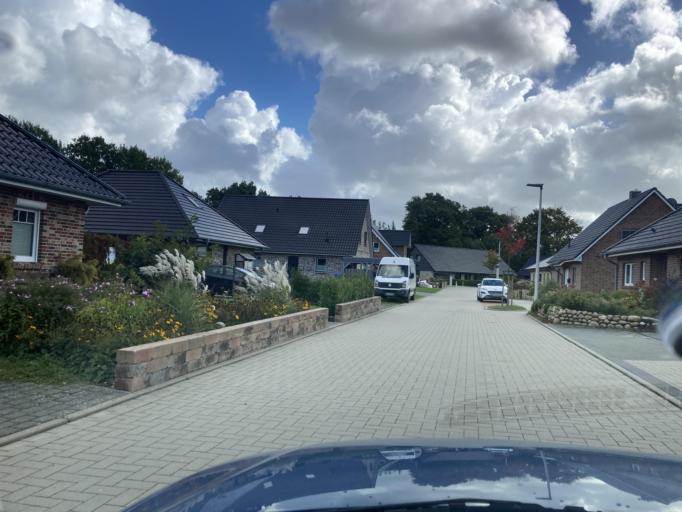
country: DE
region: Schleswig-Holstein
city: Wesseln
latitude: 54.2052
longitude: 9.0835
